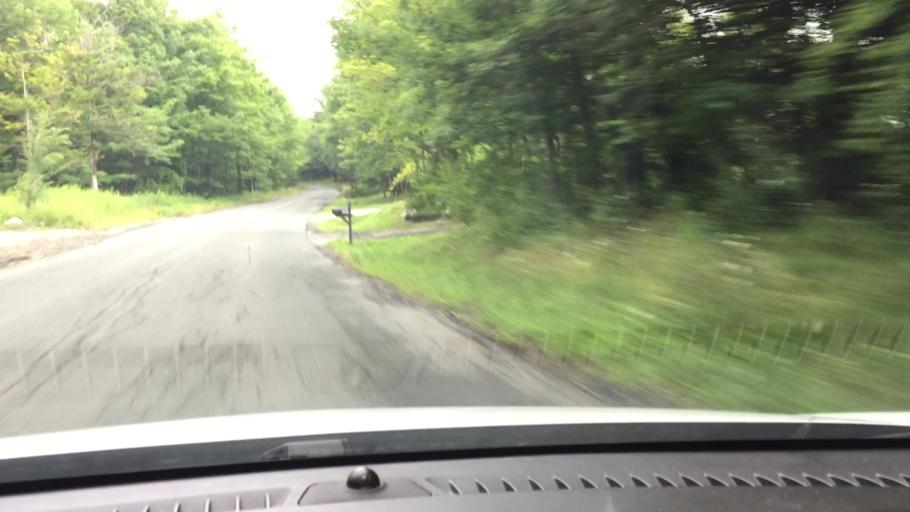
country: US
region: Massachusetts
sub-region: Berkshire County
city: Dalton
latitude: 42.4538
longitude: -73.1554
